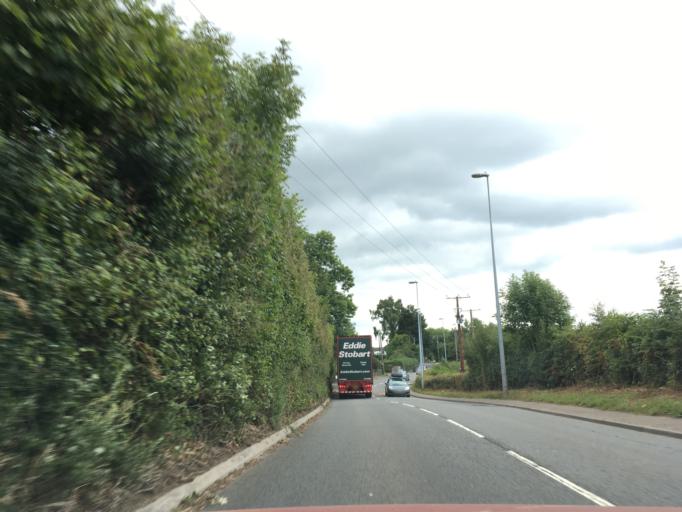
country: GB
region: Wales
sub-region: Torfaen County Borough
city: New Inn
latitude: 51.7337
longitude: -2.9862
